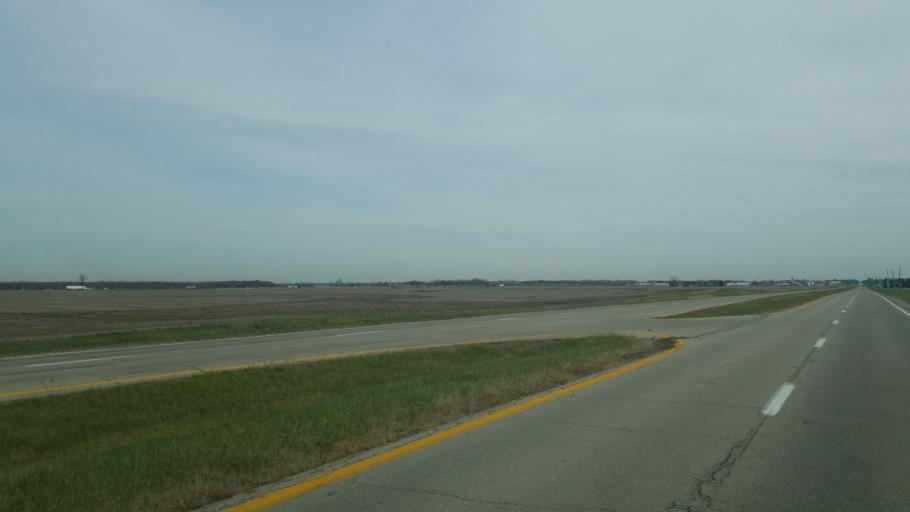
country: US
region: Ohio
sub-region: Madison County
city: Choctaw Lake
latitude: 39.9350
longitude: -83.4646
